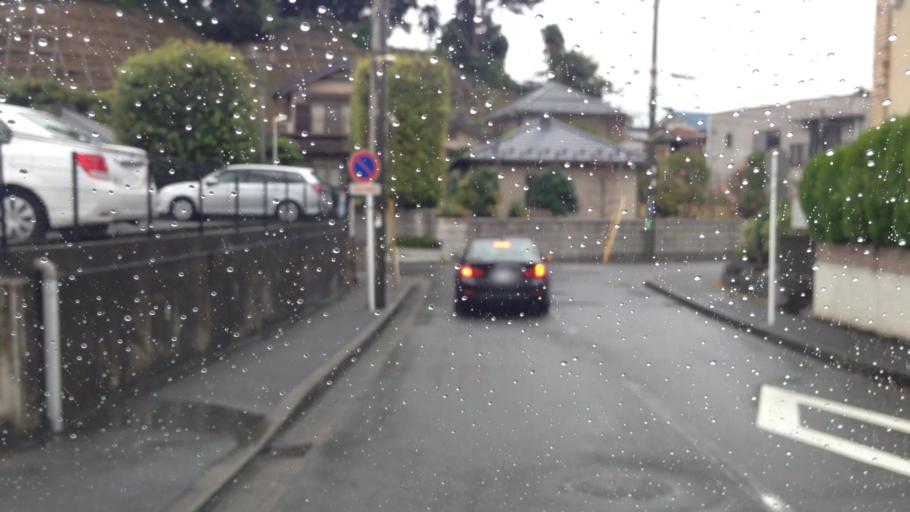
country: JP
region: Kanagawa
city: Yokohama
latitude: 35.5440
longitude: 139.5809
